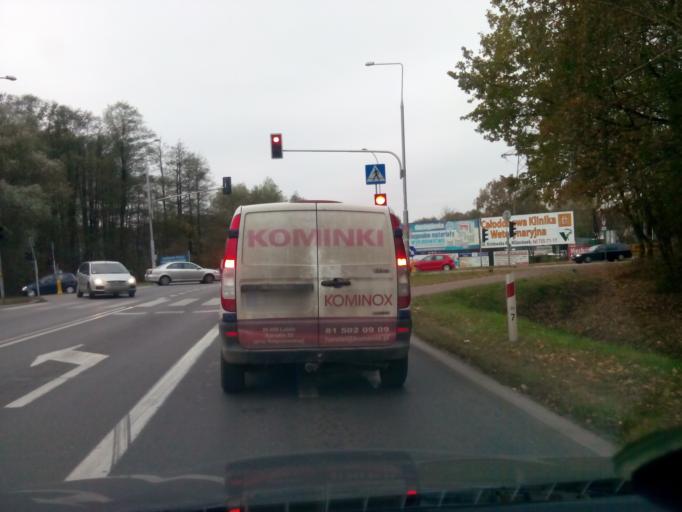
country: PL
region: Masovian Voivodeship
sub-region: Powiat grodziski
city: Podkowa Lesna
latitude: 52.1290
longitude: 20.7182
